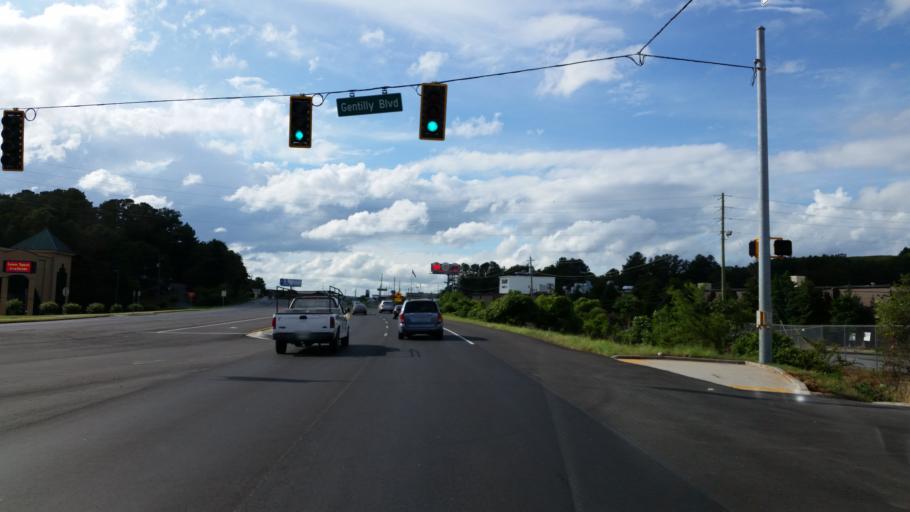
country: US
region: Georgia
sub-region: Bartow County
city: Cartersville
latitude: 34.1871
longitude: -84.7864
